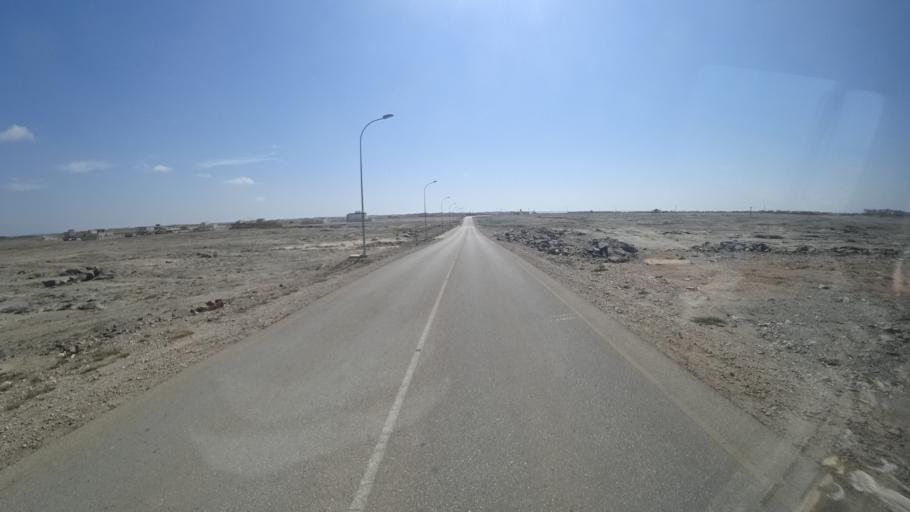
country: OM
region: Zufar
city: Salalah
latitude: 16.9676
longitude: 54.7331
